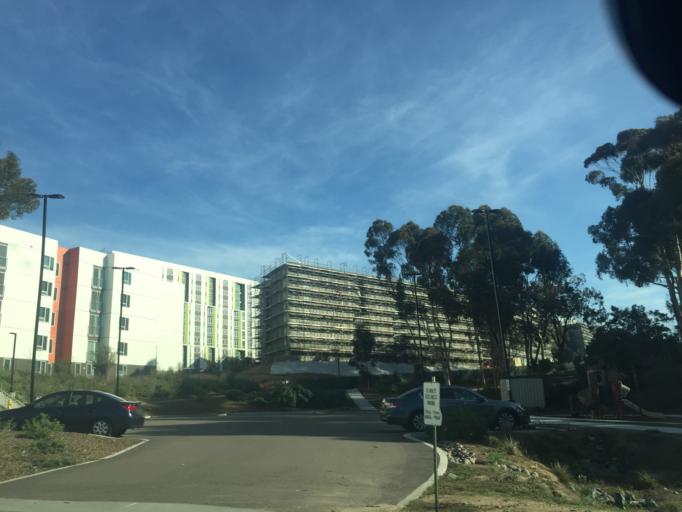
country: US
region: California
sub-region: San Diego County
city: La Jolla
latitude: 32.8741
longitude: -117.2226
